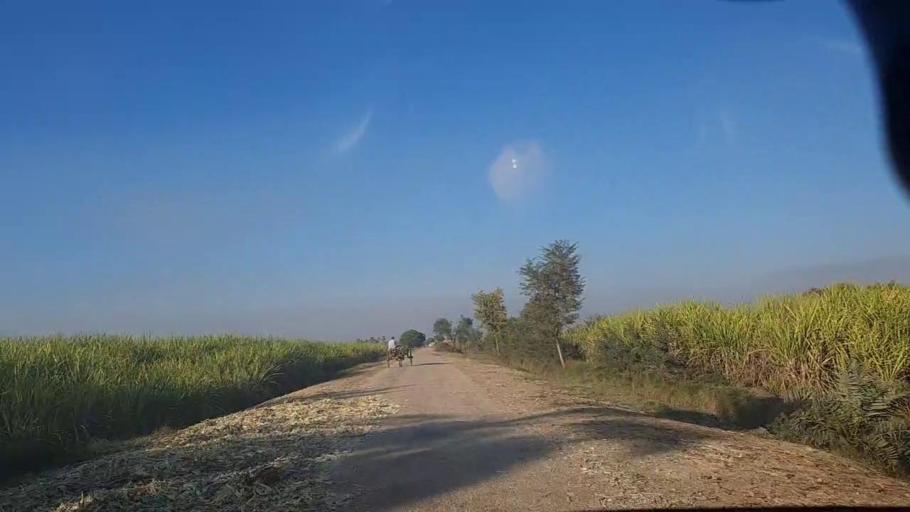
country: PK
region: Sindh
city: Sobhadero
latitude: 27.4114
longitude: 68.4225
